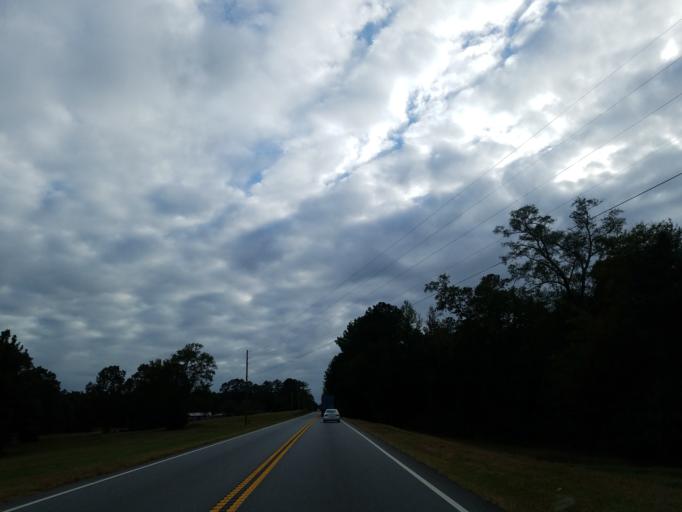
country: US
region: Georgia
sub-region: Lamar County
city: Barnesville
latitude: 33.1820
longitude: -84.0807
